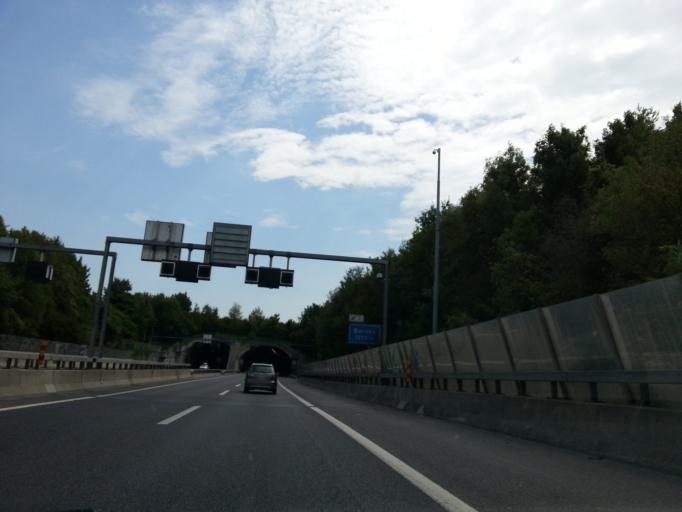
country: CH
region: Geneva
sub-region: Geneva
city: Vernier
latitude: 46.2017
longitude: 6.0765
